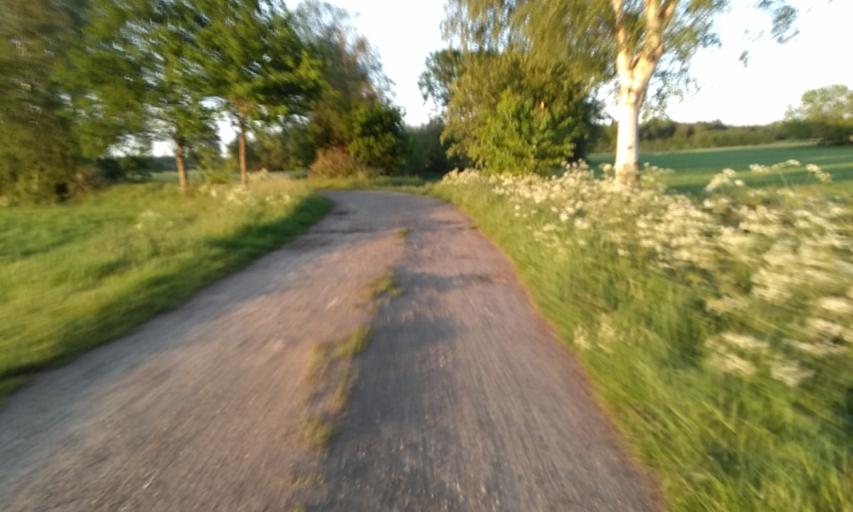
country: DE
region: Lower Saxony
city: Ahlerstedt
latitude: 53.4308
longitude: 9.4313
